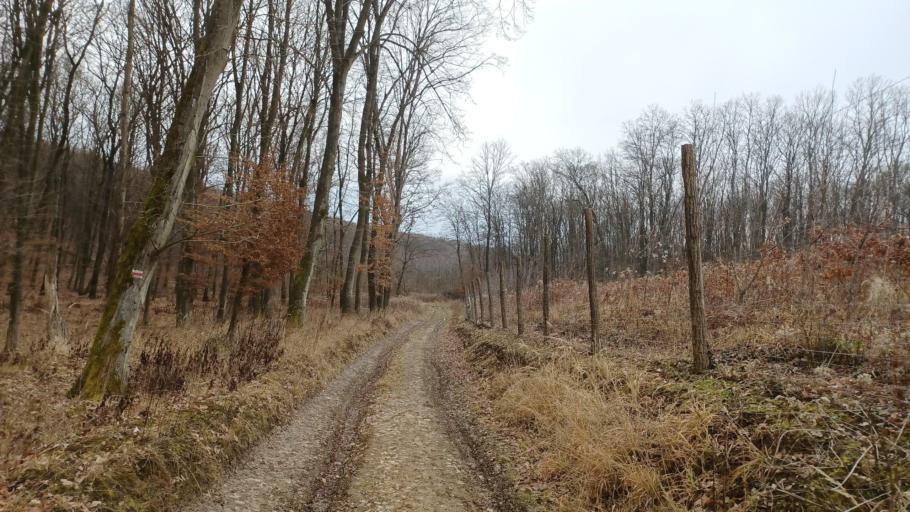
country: HU
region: Tolna
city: Szentgalpuszta
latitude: 46.3051
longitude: 18.6403
